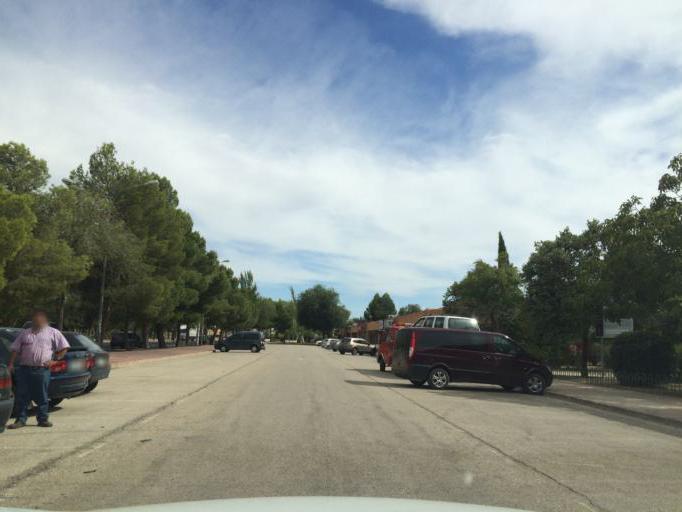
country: ES
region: Castille-La Mancha
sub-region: Provincia de Albacete
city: Albacete
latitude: 39.0129
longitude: -1.8787
